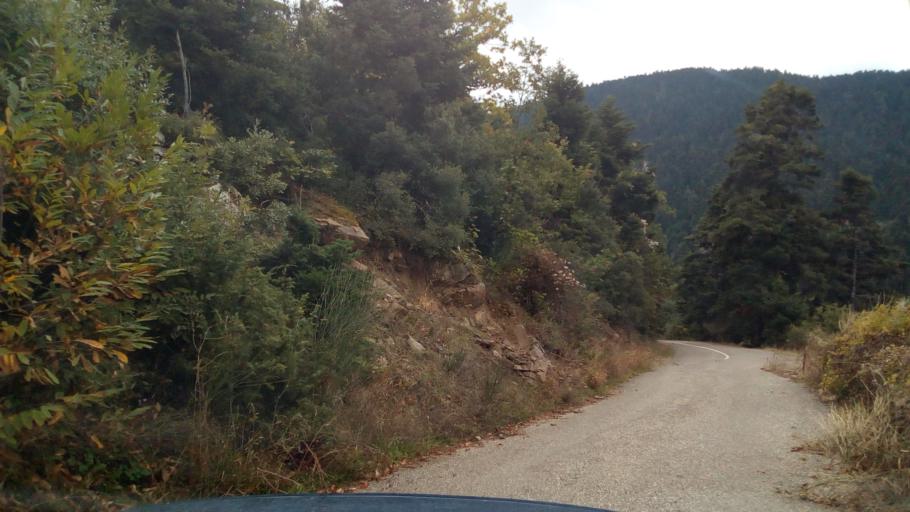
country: GR
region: Central Greece
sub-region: Nomos Fokidos
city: Lidoriki
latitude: 38.4780
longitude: 22.0722
